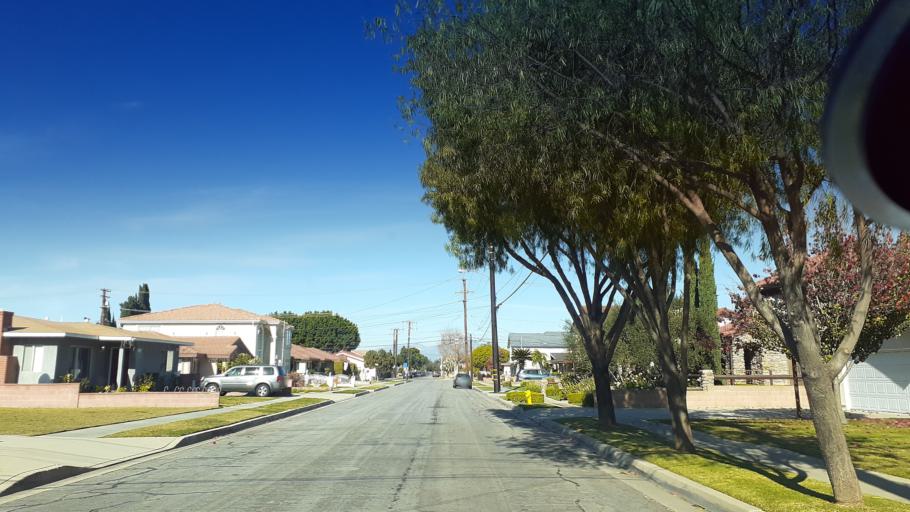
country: US
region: California
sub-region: Los Angeles County
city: Artesia
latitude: 33.8615
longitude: -118.0756
